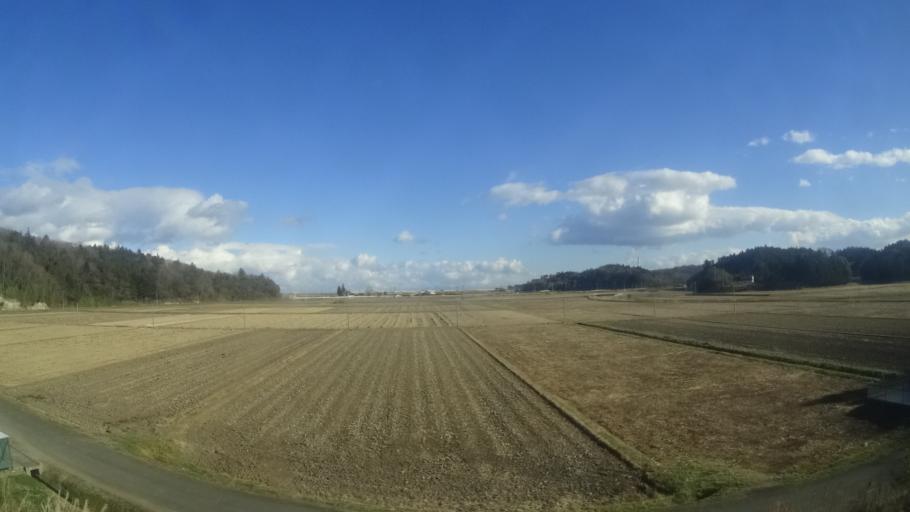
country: JP
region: Fukushima
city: Namie
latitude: 37.6858
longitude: 140.9727
